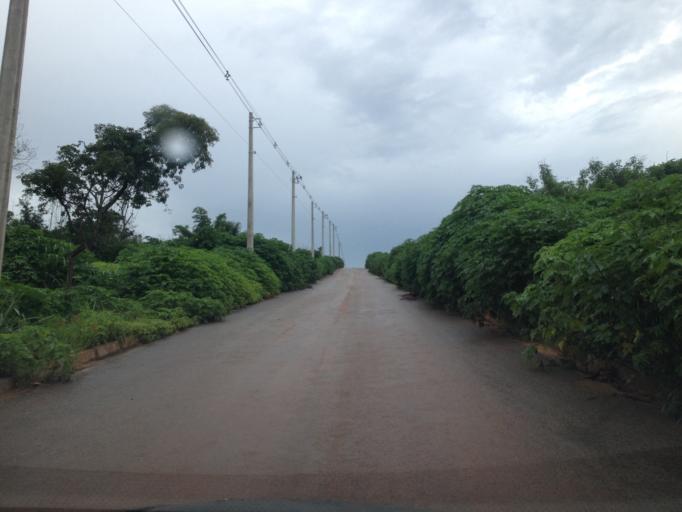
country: BR
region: Goias
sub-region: Luziania
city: Luziania
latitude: -16.0602
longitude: -47.9645
